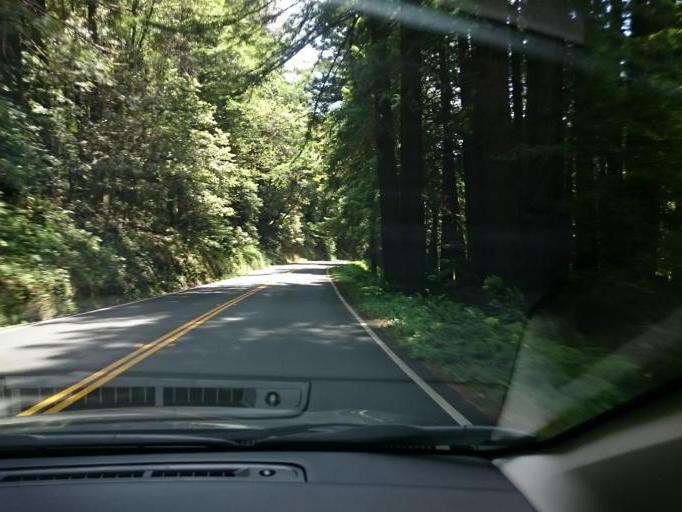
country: US
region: California
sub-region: Mendocino County
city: Fort Bragg
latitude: 39.1816
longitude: -123.7125
